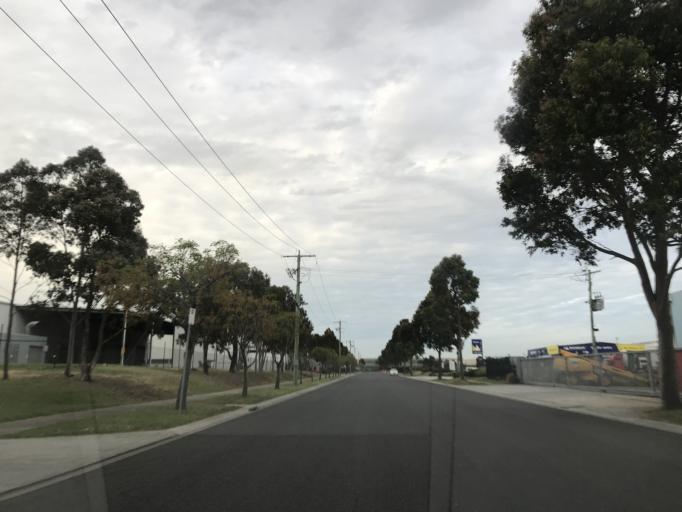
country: AU
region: Victoria
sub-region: Brimbank
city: Derrimut
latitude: -37.8090
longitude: 144.7814
